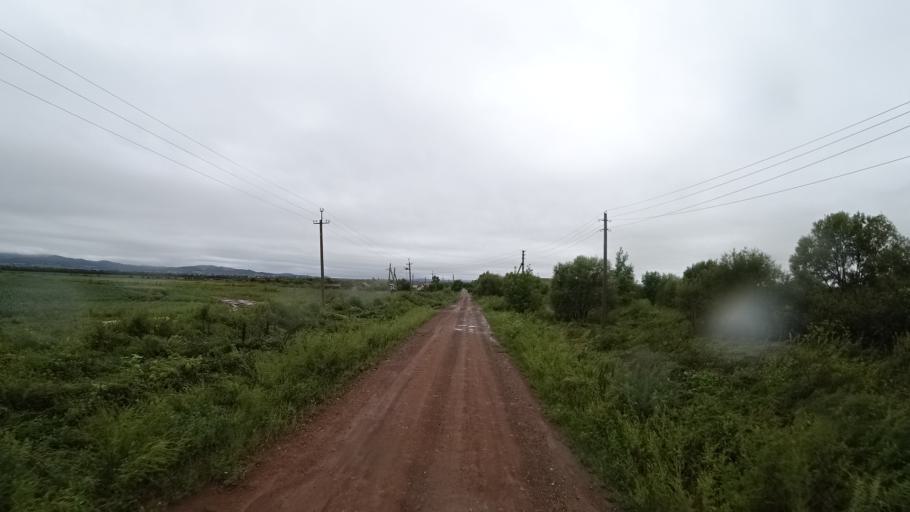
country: RU
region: Primorskiy
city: Monastyrishche
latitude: 44.2334
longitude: 132.4634
